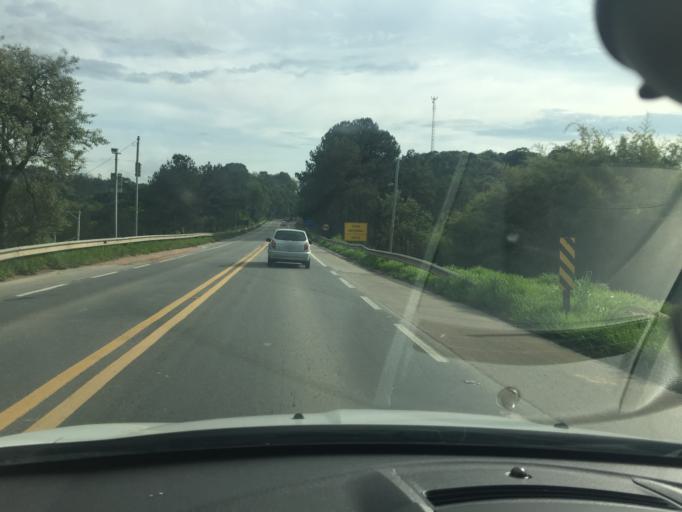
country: BR
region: Sao Paulo
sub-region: Campo Limpo Paulista
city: Campo Limpo Paulista
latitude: -23.1755
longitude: -46.7745
